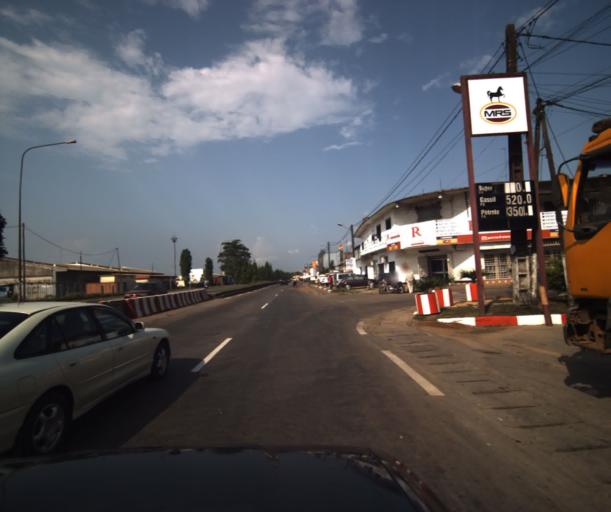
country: CM
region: Littoral
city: Douala
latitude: 4.0561
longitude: 9.6954
